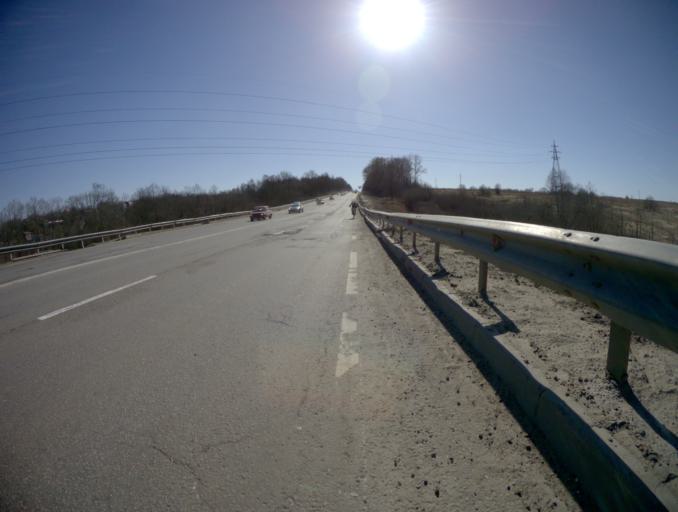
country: RU
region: Vladimir
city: Bogolyubovo
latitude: 56.1818
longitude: 40.5092
